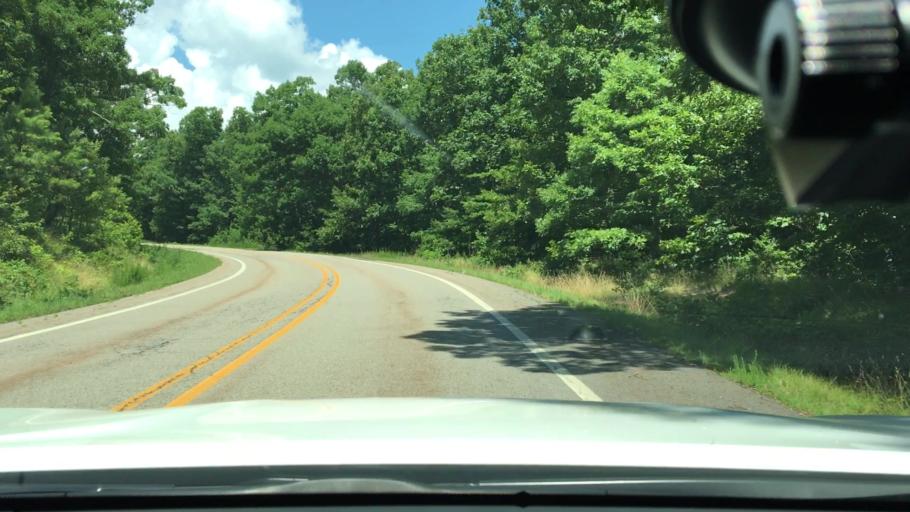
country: US
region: Arkansas
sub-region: Logan County
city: Paris
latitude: 35.1703
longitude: -93.6425
